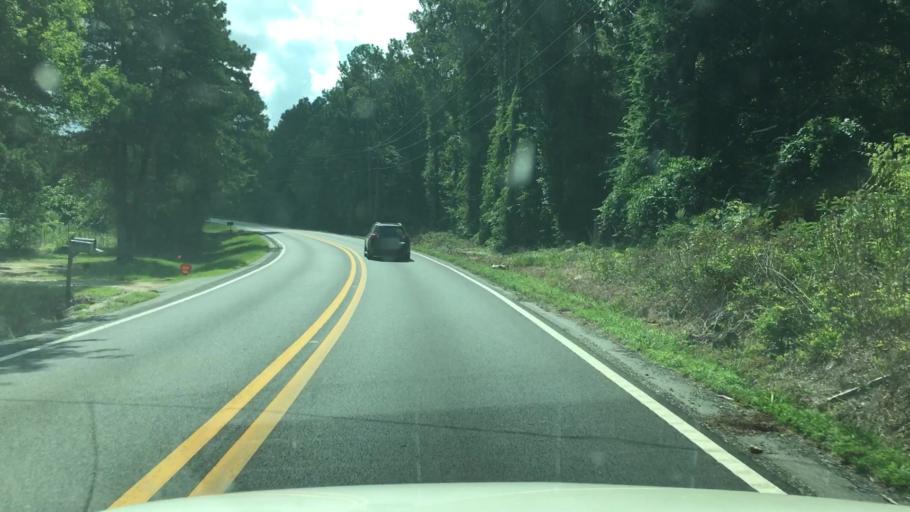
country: US
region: Arkansas
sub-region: Clark County
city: Arkadelphia
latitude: 34.2501
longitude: -93.1199
